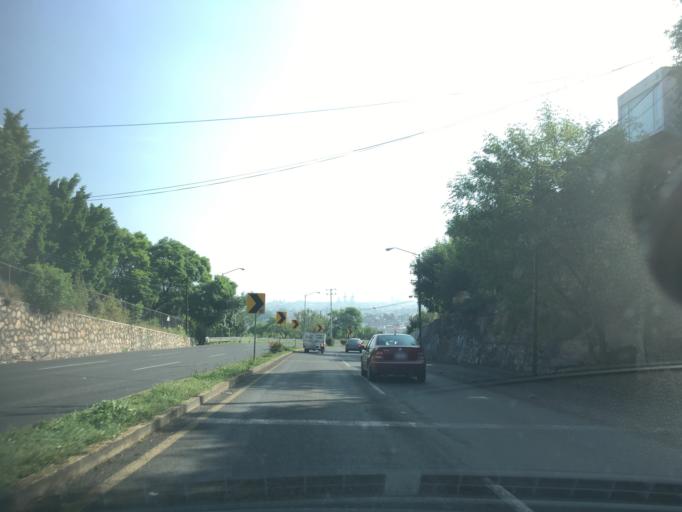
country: MX
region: Michoacan
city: Morelia
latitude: 19.6795
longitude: -101.2014
